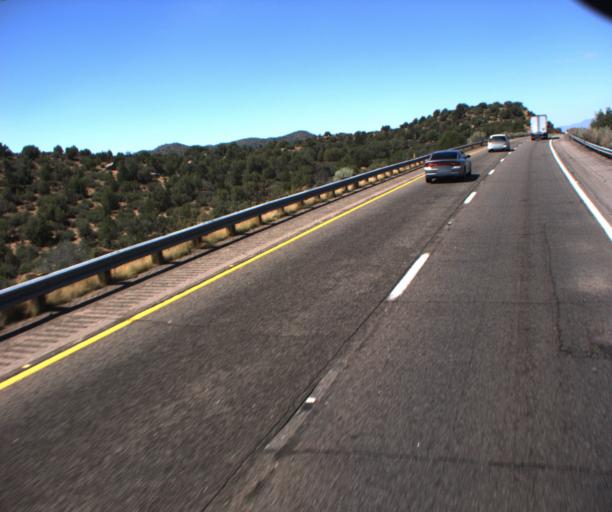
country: US
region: Arizona
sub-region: Mohave County
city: Peach Springs
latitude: 35.1813
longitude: -113.4743
